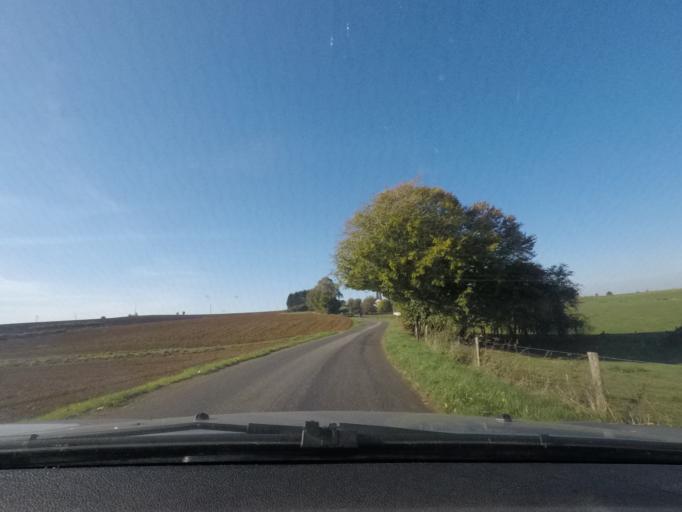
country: BE
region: Wallonia
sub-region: Province du Luxembourg
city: Musson
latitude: 49.6221
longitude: 5.7310
